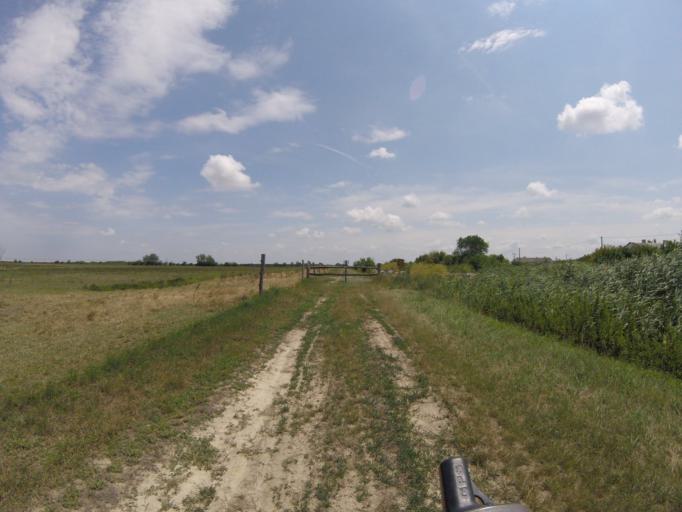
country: HU
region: Hajdu-Bihar
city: Hortobagy
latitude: 47.6077
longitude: 21.0734
